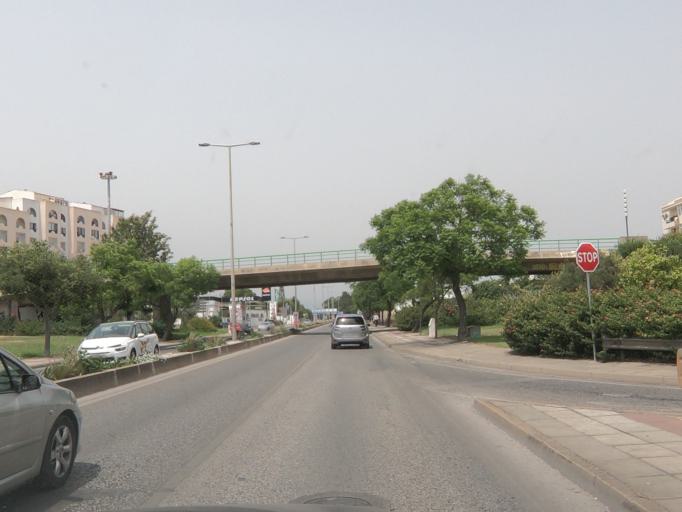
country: PT
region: Faro
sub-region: Portimao
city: Portimao
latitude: 37.1363
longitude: -8.5457
